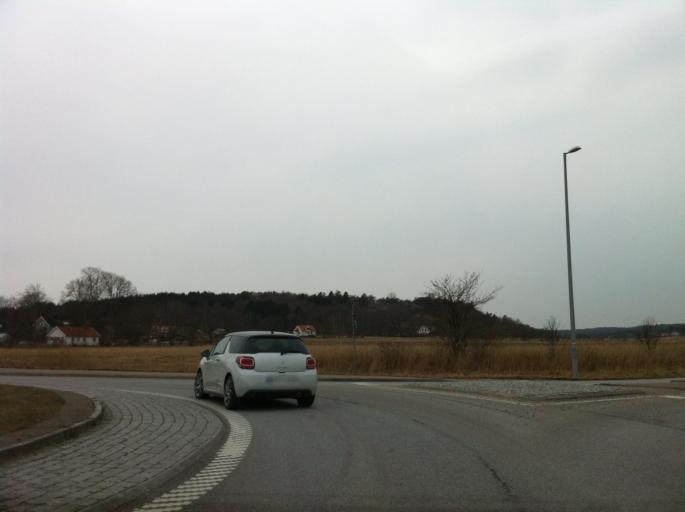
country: SE
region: Vaestra Goetaland
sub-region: Orust
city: Henan
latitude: 58.2113
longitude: 11.6915
